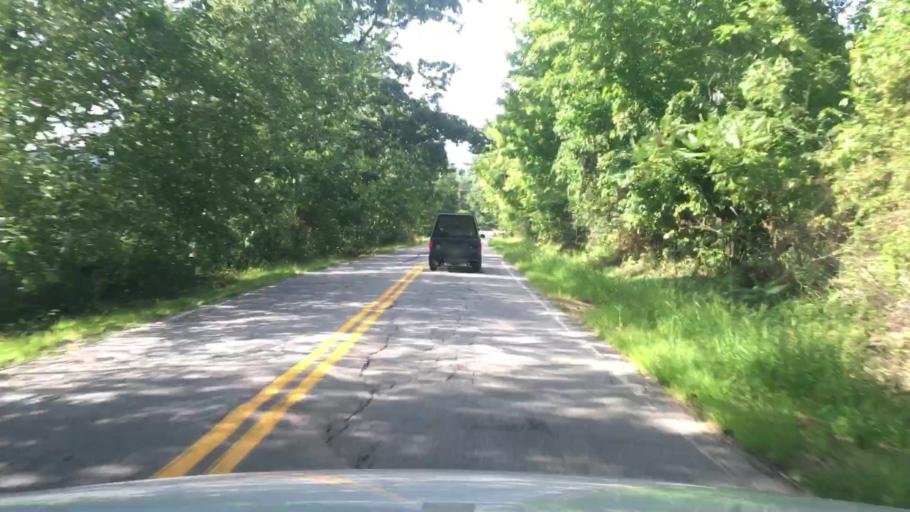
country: US
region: New Hampshire
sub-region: Belknap County
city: Gilford
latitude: 43.5630
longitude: -71.4140
